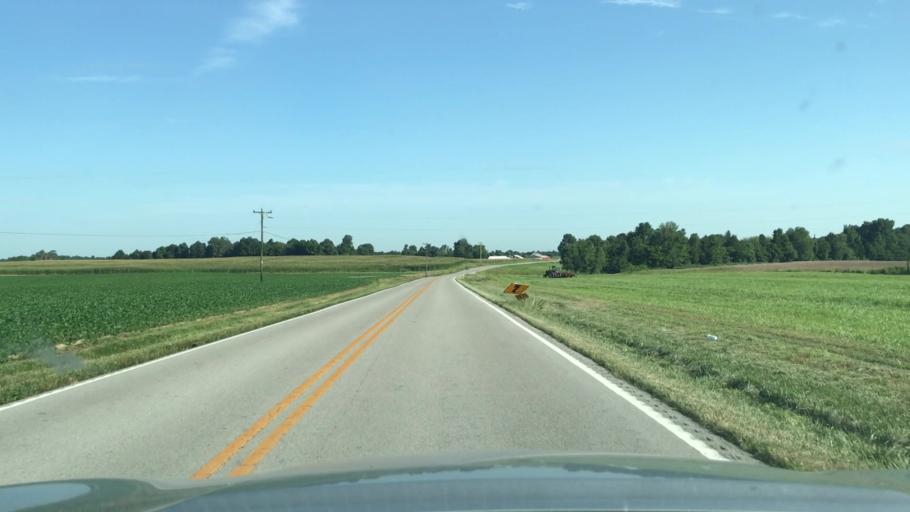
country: US
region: Kentucky
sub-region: Muhlenberg County
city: Greenville
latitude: 37.0170
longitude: -87.1320
